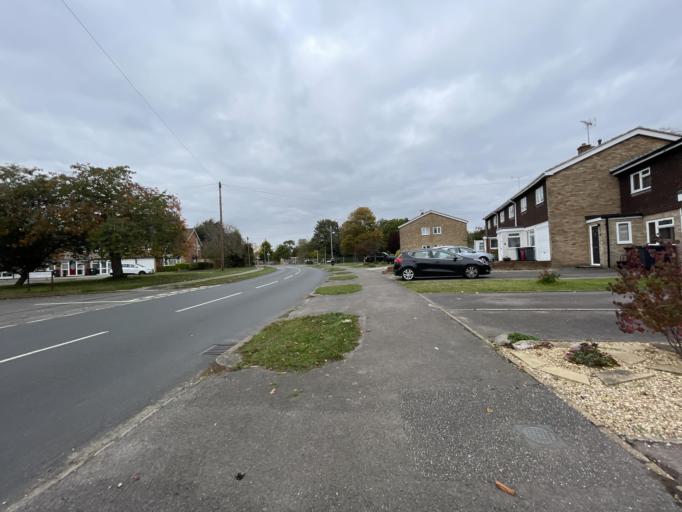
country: GB
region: England
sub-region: West Berkshire
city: Tilehurst
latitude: 51.4576
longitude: -1.0370
